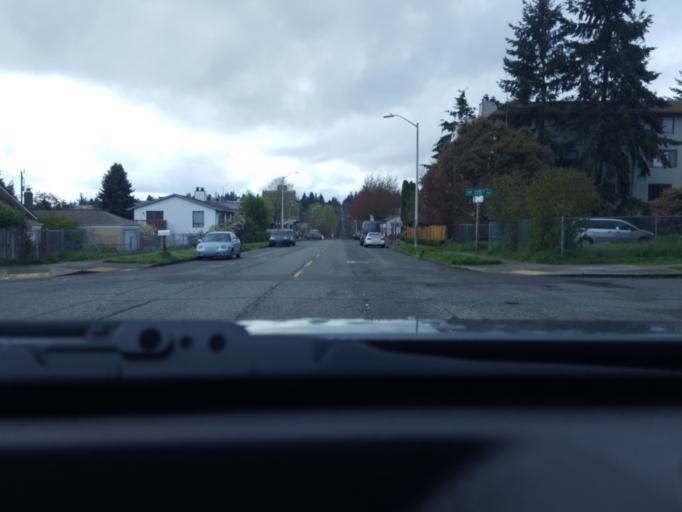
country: US
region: Washington
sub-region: King County
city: Shoreline
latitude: 47.7125
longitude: -122.3180
